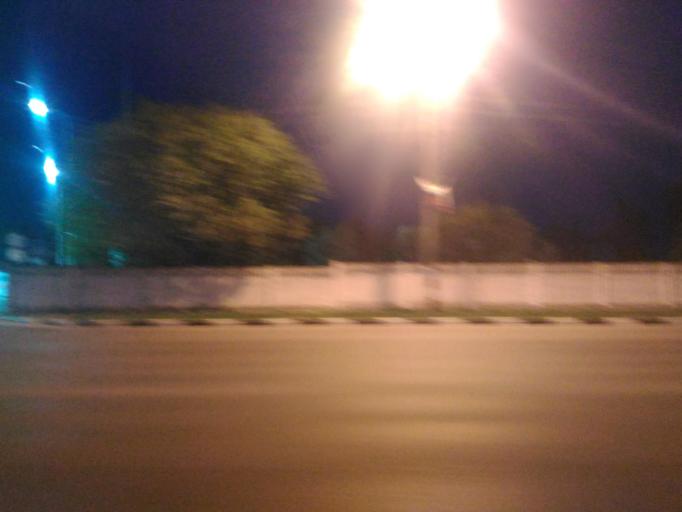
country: RU
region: Ulyanovsk
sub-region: Ulyanovskiy Rayon
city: Ulyanovsk
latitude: 54.2851
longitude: 48.3567
